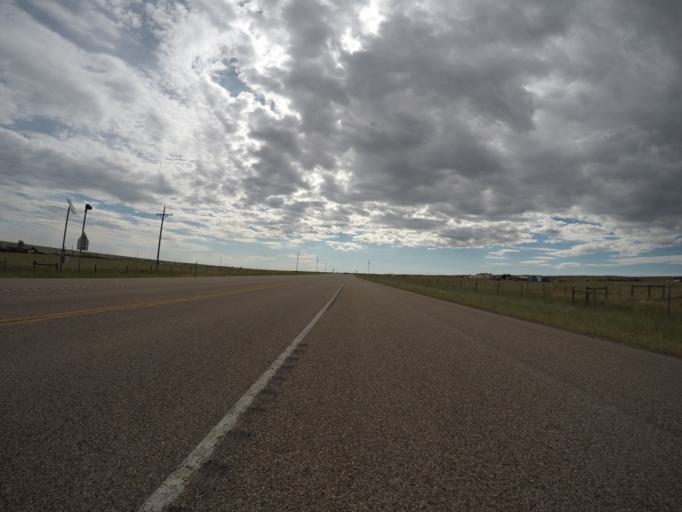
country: US
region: Wyoming
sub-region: Laramie County
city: Cheyenne
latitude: 41.1566
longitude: -105.0731
